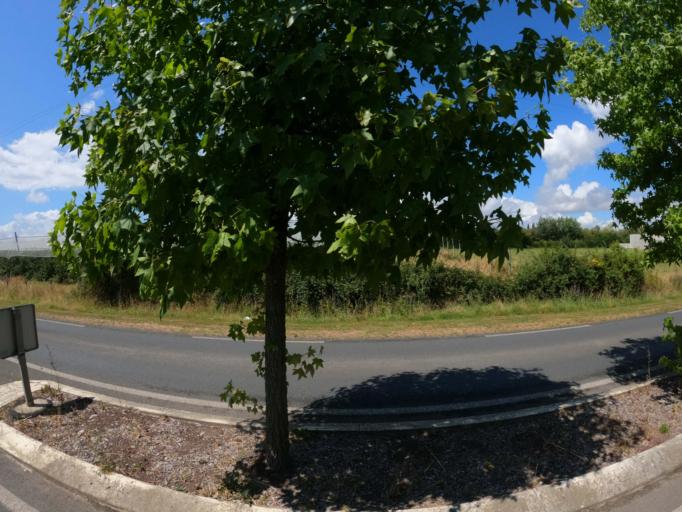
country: FR
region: Pays de la Loire
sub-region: Departement de Maine-et-Loire
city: Champigne
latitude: 47.6574
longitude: -0.5745
